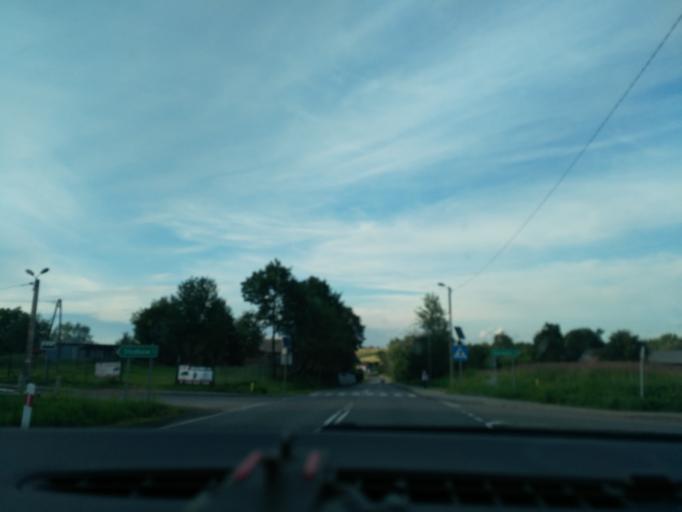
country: PL
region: Lublin Voivodeship
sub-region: Powiat krasnicki
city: Krasnik
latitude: 50.9000
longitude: 22.2701
